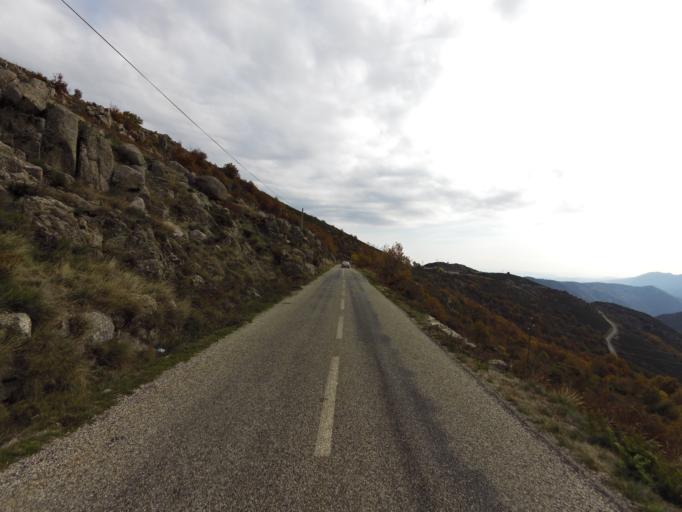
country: FR
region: Rhone-Alpes
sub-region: Departement de l'Ardeche
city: Les Vans
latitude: 44.5099
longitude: 4.0403
